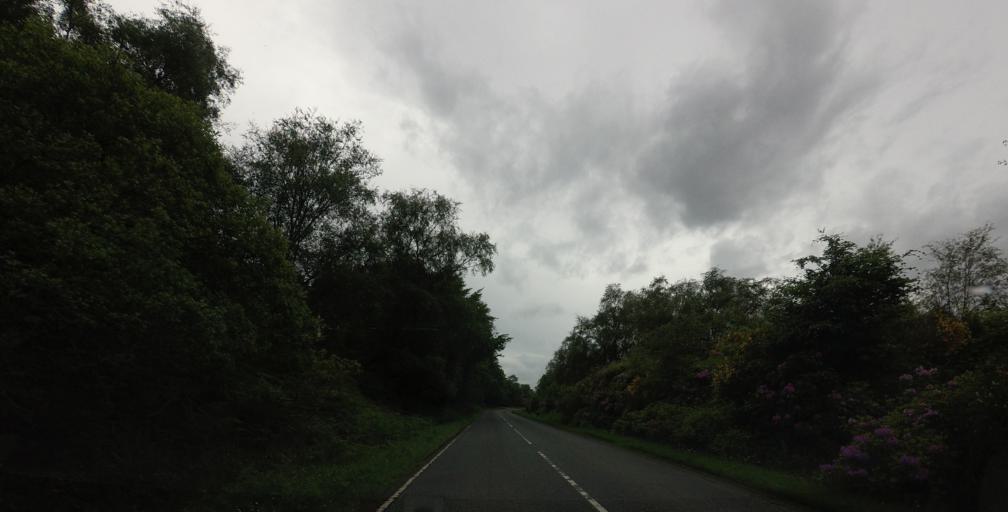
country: GB
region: Scotland
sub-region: Highland
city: Fort William
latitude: 56.7126
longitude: -5.2747
